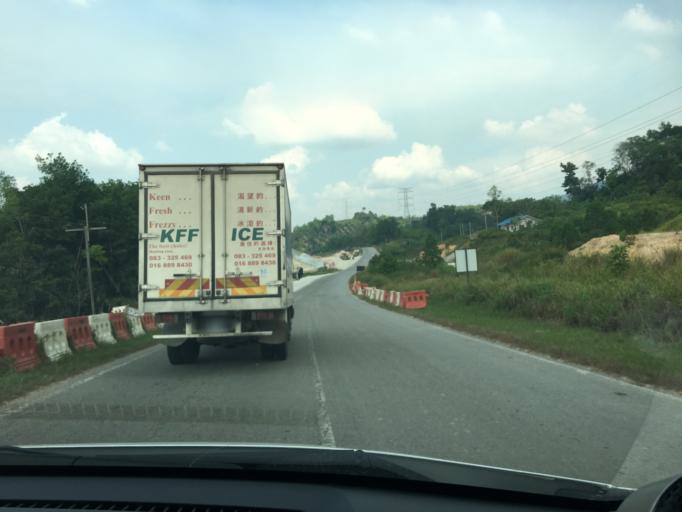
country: MY
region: Sarawak
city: Simanggang
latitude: 1.0698
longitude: 111.2980
